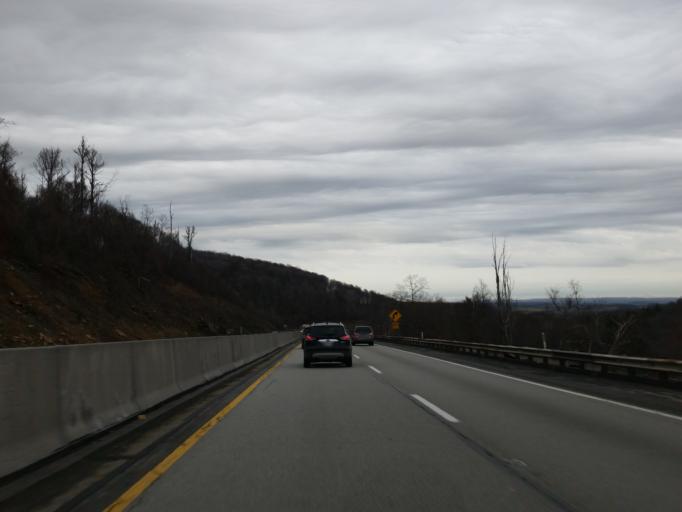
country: US
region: Pennsylvania
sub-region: Somerset County
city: Somerset
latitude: 40.0840
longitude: -79.1930
